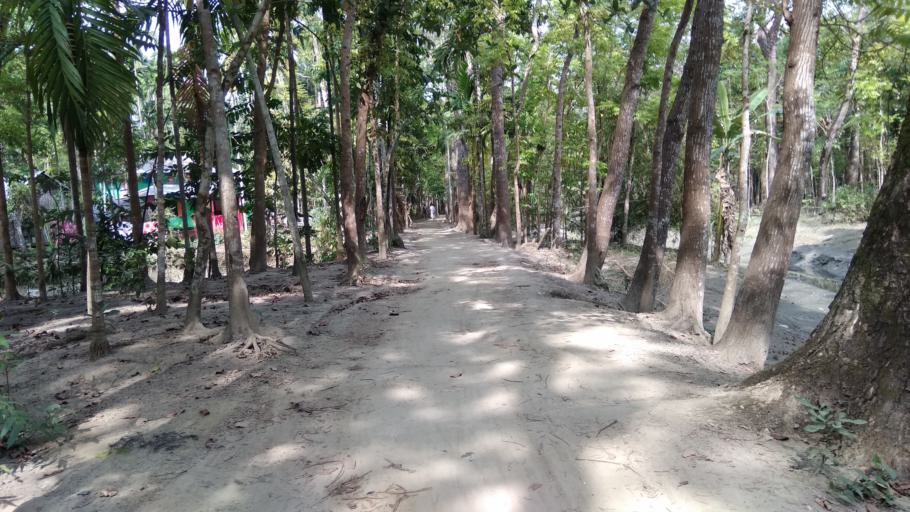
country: BD
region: Barisal
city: Gaurnadi
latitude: 22.9923
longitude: 90.3720
